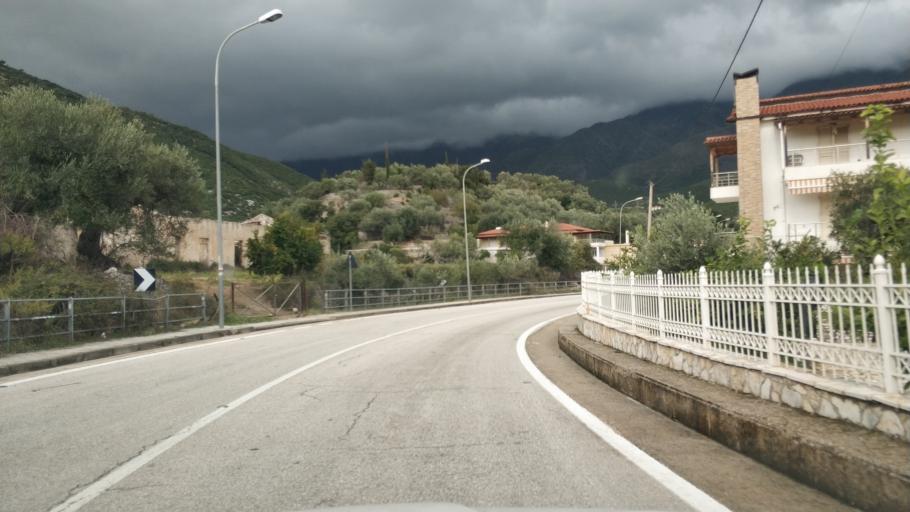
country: AL
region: Vlore
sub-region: Rrethi i Vlores
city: Himare
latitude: 40.1210
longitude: 19.7328
